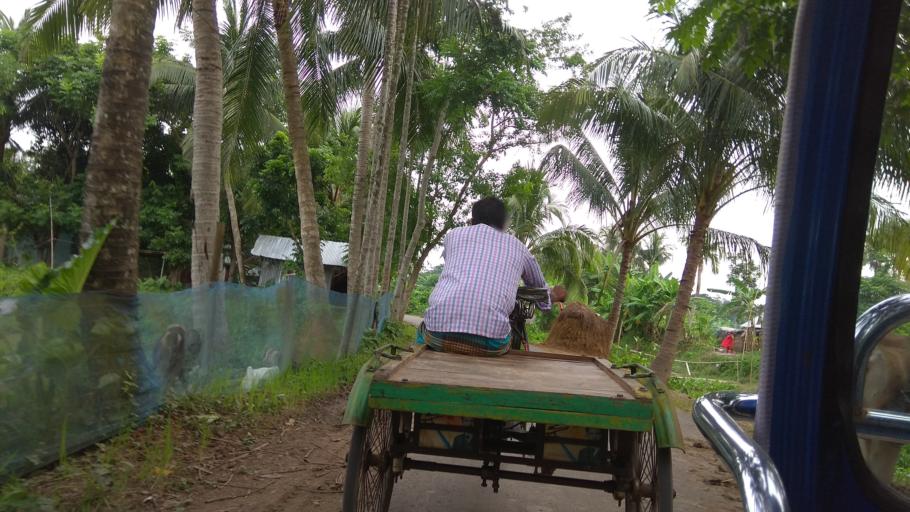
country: BD
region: Khulna
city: Kalia
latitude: 23.0297
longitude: 89.6459
